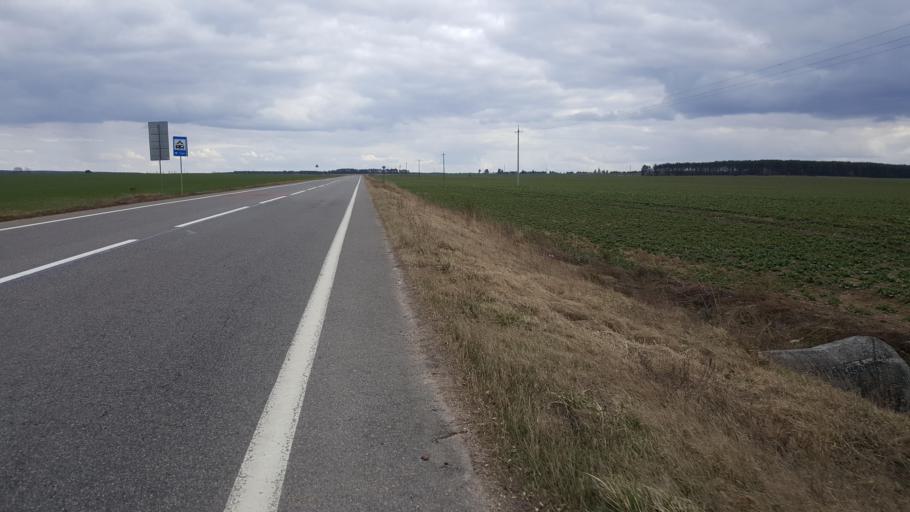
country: BY
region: Brest
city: Kamyanyets
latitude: 52.4205
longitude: 23.8432
